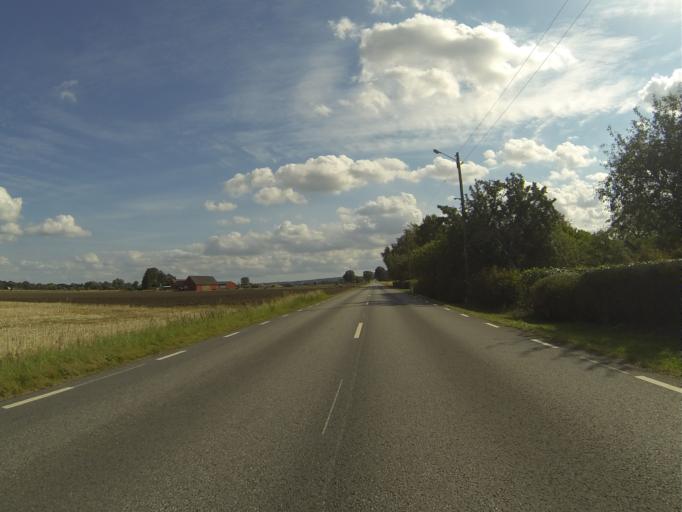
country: SE
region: Skane
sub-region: Eslovs Kommun
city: Eslov
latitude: 55.7491
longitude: 13.3244
